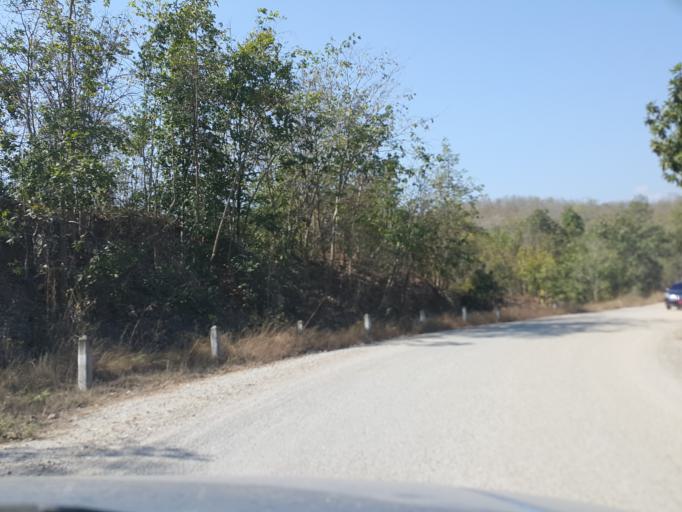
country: TH
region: Chiang Mai
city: Doi Lo
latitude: 18.5253
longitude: 98.7538
